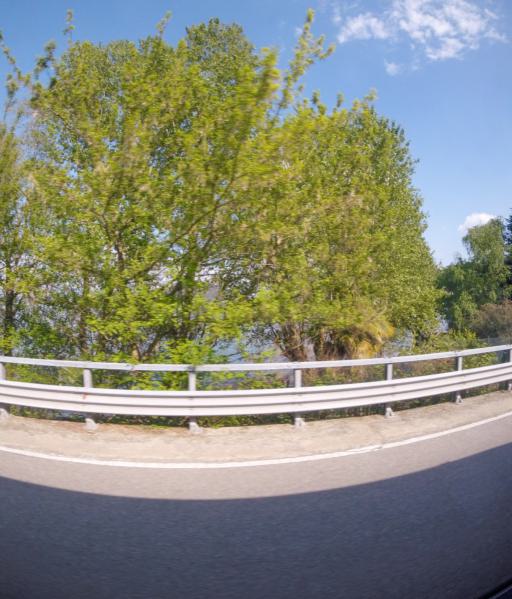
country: IT
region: Piedmont
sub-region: Provincia di Novara
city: Meina
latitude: 45.7812
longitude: 8.5420
